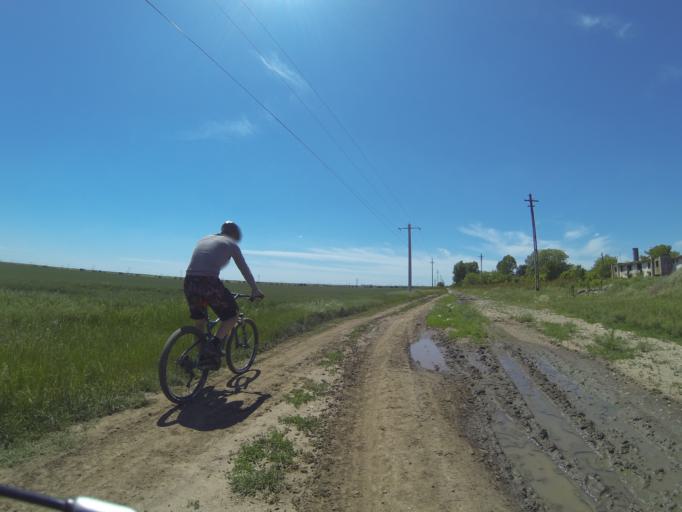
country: RO
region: Dolj
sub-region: Comuna Leu
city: Leu
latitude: 44.1985
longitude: 24.0565
